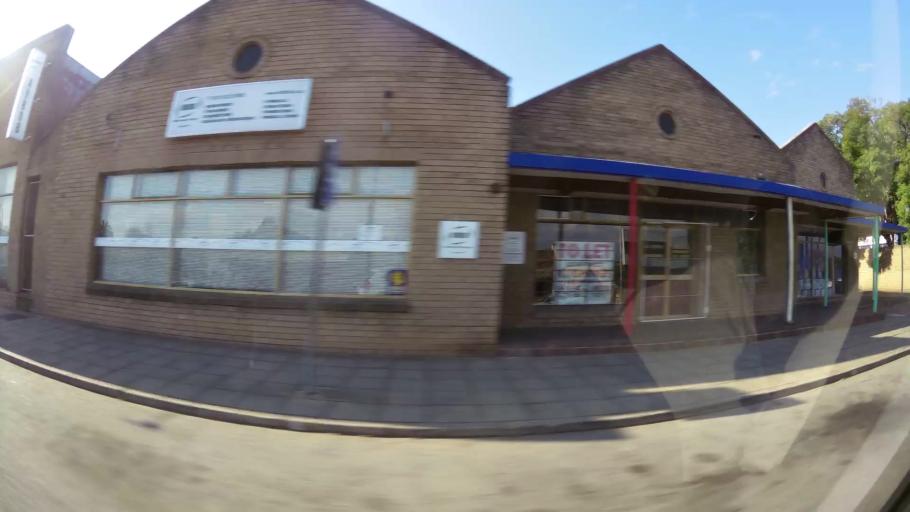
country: ZA
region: Eastern Cape
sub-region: Nelson Mandela Bay Metropolitan Municipality
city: Uitenhage
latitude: -33.7635
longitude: 25.3951
